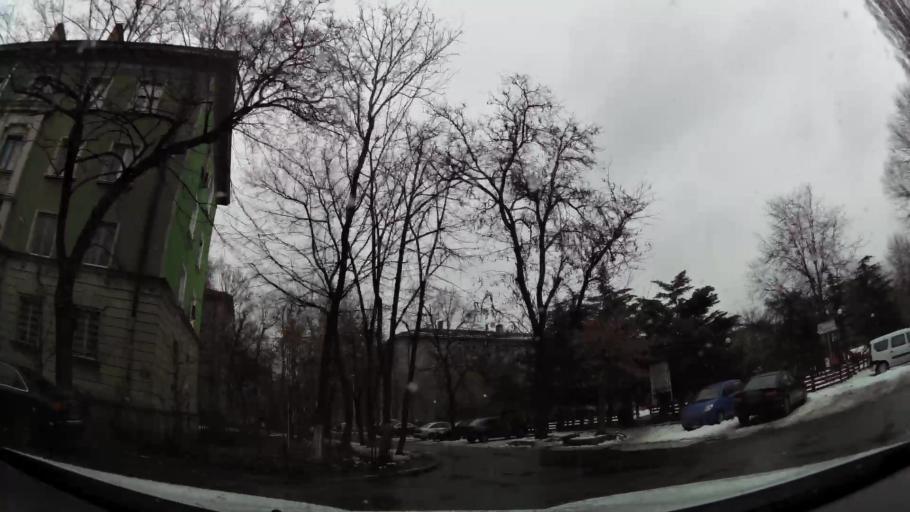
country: RO
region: Bucuresti
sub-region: Municipiul Bucuresti
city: Bucuresti
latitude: 44.4276
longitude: 26.0560
